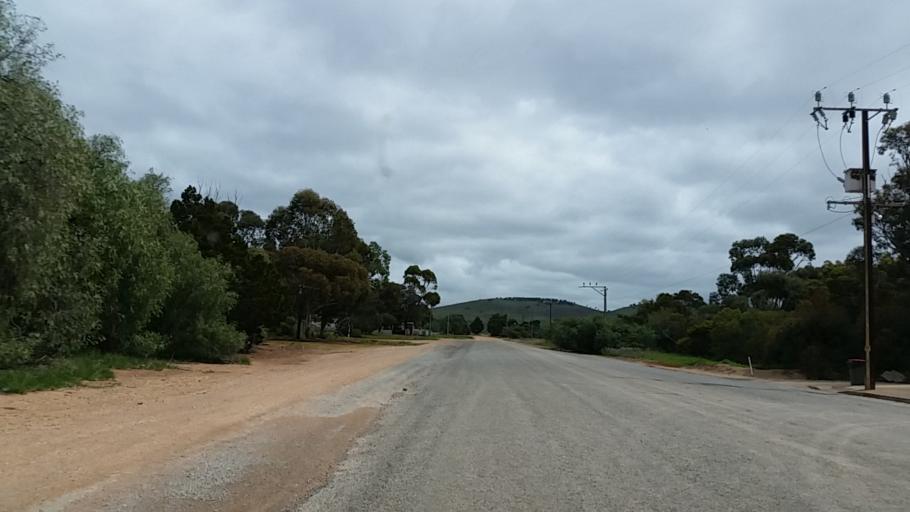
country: AU
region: South Australia
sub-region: Wakefield
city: Balaklava
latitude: -33.9275
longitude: 138.1613
